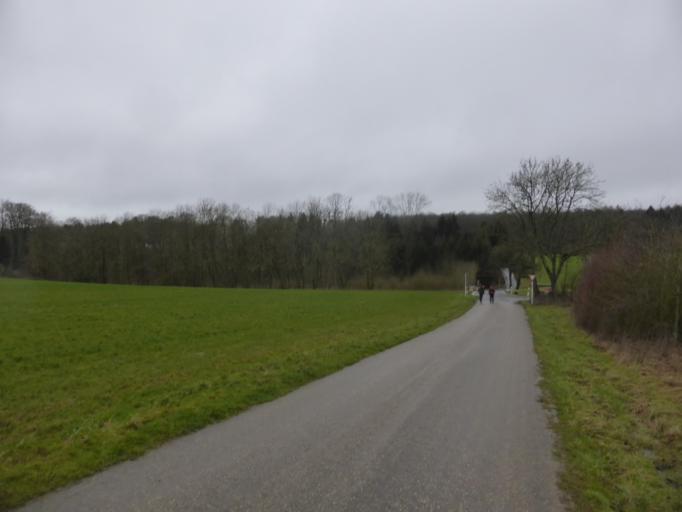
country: LU
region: Luxembourg
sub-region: Canton de Mersch
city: Fischbach
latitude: 49.7254
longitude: 6.1685
